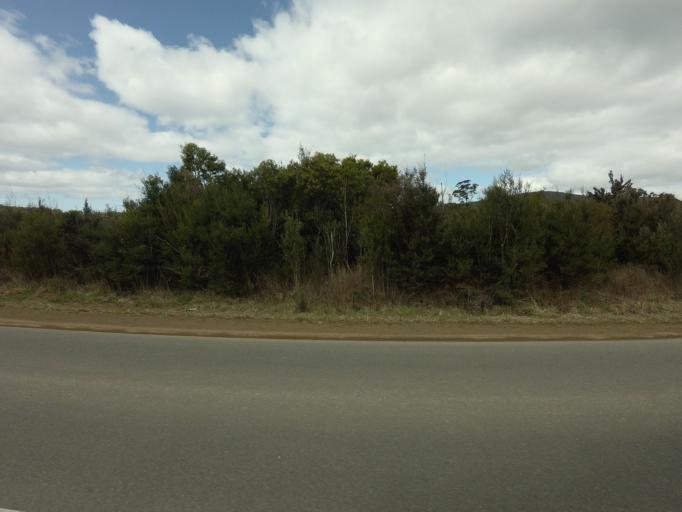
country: AU
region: Tasmania
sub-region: Huon Valley
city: Geeveston
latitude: -43.3267
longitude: 146.9718
